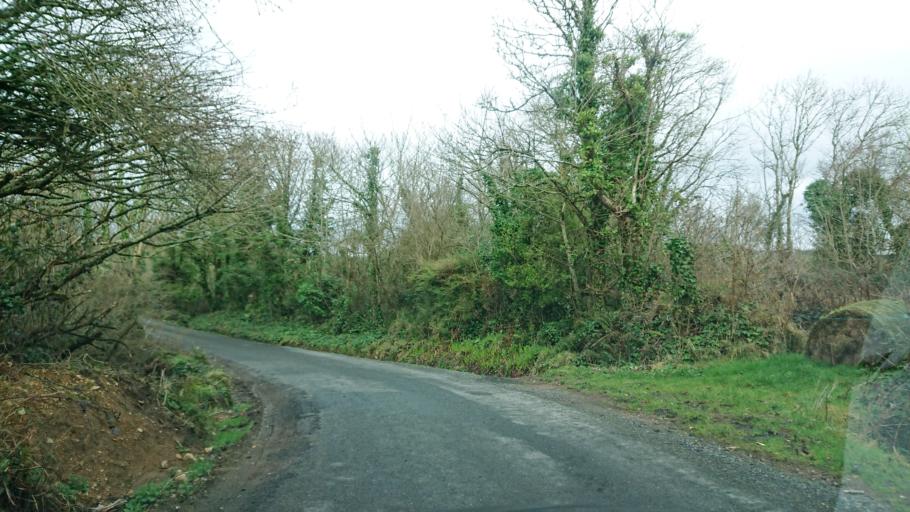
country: IE
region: Munster
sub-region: Waterford
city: Dunmore East
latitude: 52.1670
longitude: -7.0402
